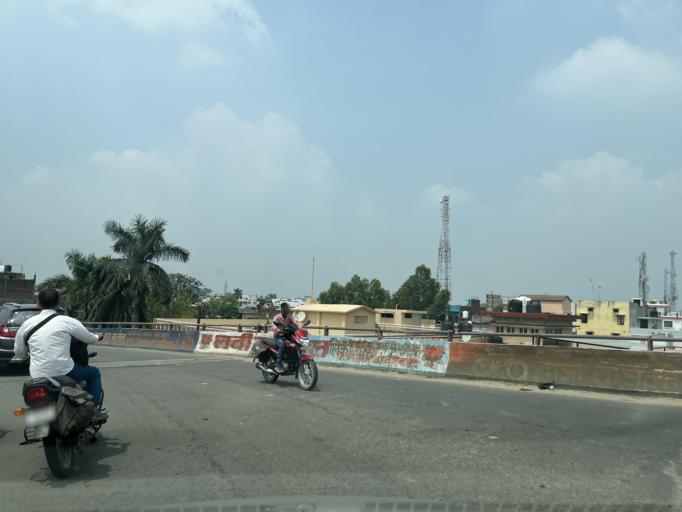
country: IN
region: Uttar Pradesh
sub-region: Bijnor
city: Najibabad
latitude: 29.6056
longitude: 78.3432
